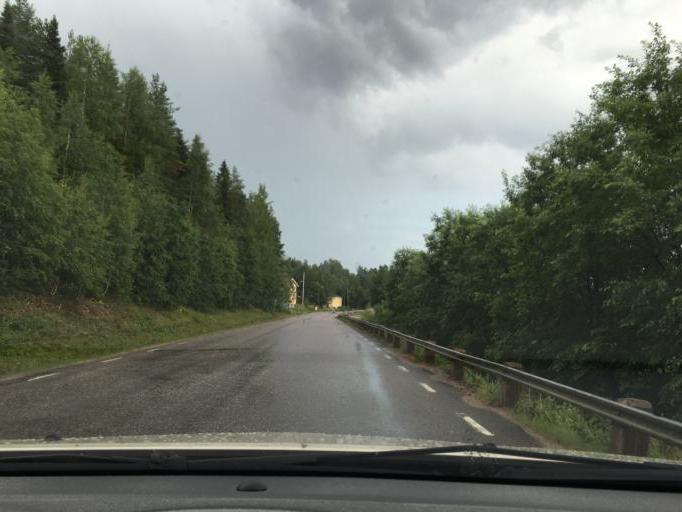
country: SE
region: Norrbotten
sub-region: Kalix Kommun
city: Rolfs
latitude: 65.9320
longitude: 22.8939
